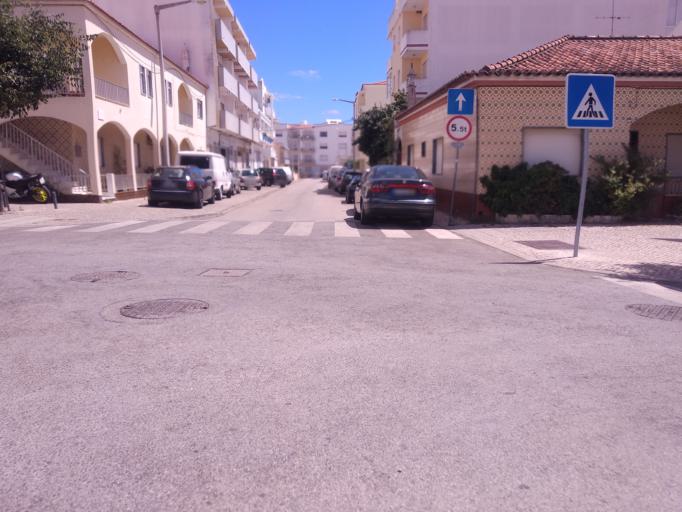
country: PT
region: Faro
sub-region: Sao Bras de Alportel
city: Sao Bras de Alportel
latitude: 37.1528
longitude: -7.8828
